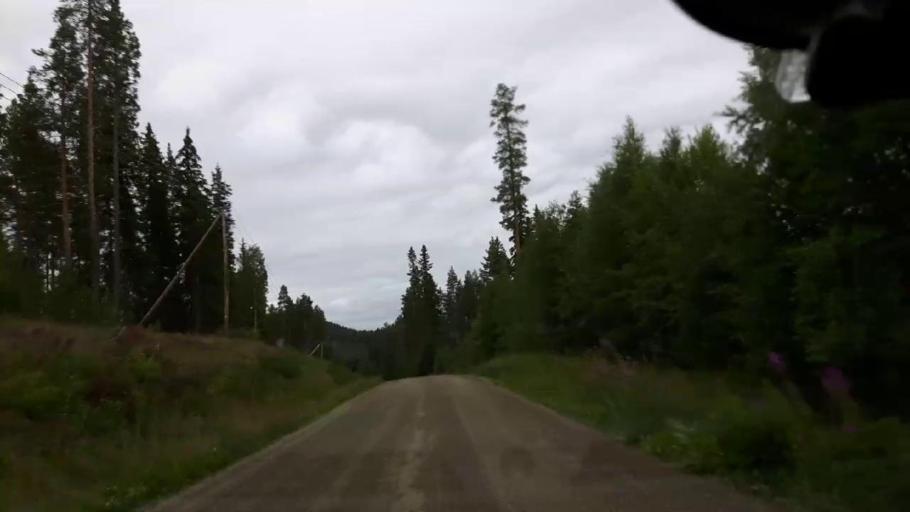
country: SE
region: Jaemtland
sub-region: Braecke Kommun
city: Braecke
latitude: 63.0090
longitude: 15.3807
